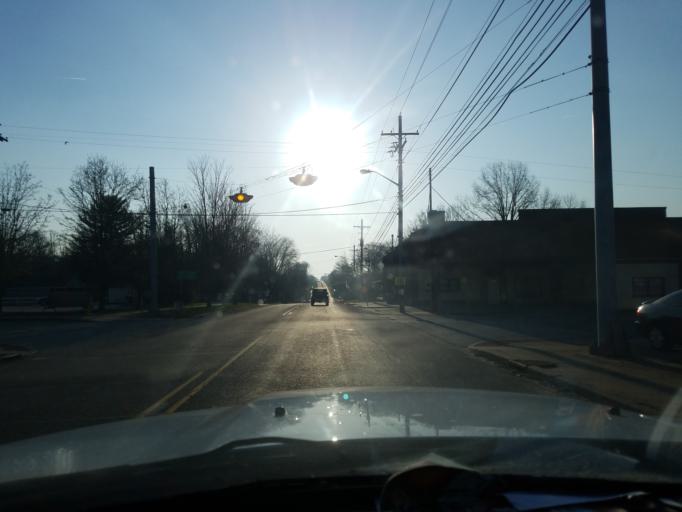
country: US
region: Indiana
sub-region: Vigo County
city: Seelyville
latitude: 39.3903
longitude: -87.2980
